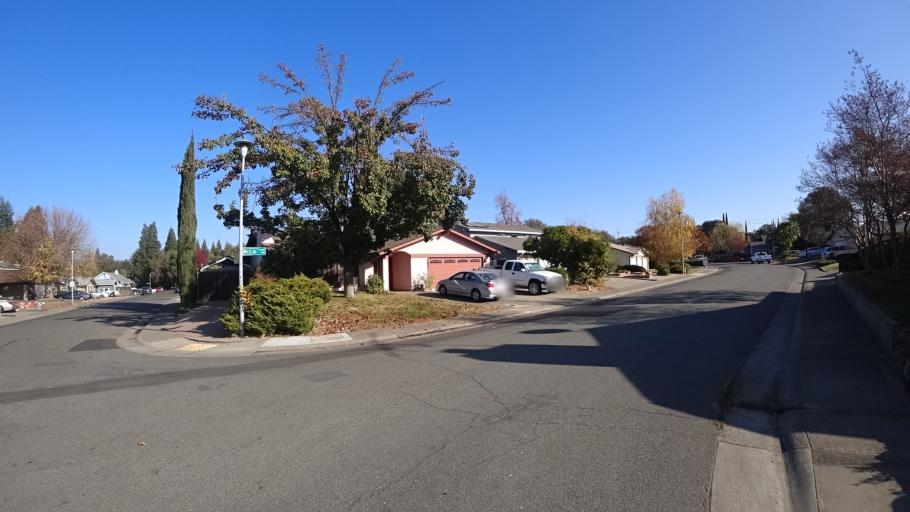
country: US
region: California
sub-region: Sacramento County
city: Citrus Heights
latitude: 38.6964
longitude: -121.2736
